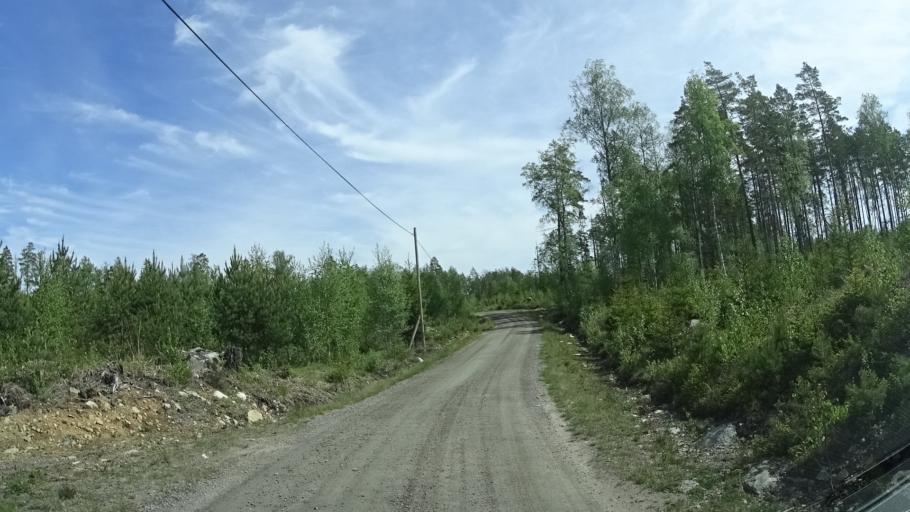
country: SE
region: OEstergoetland
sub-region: Finspangs Kommun
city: Finspang
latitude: 58.7776
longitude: 15.8536
